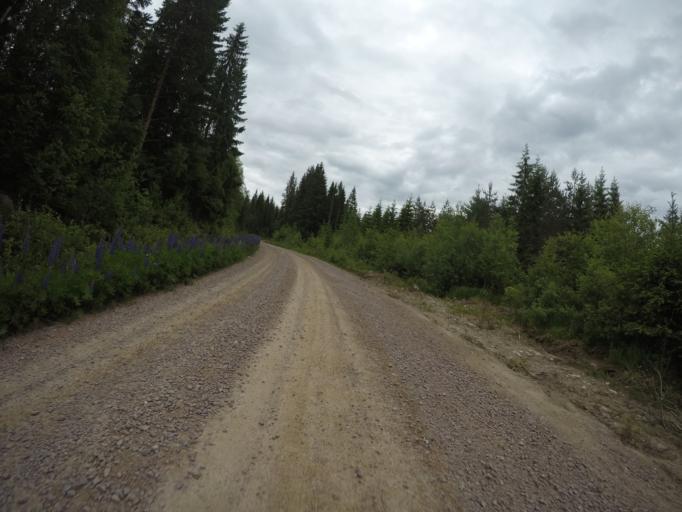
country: SE
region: Dalarna
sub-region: Ludvika Kommun
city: Abborrberget
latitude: 60.1043
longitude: 14.5217
